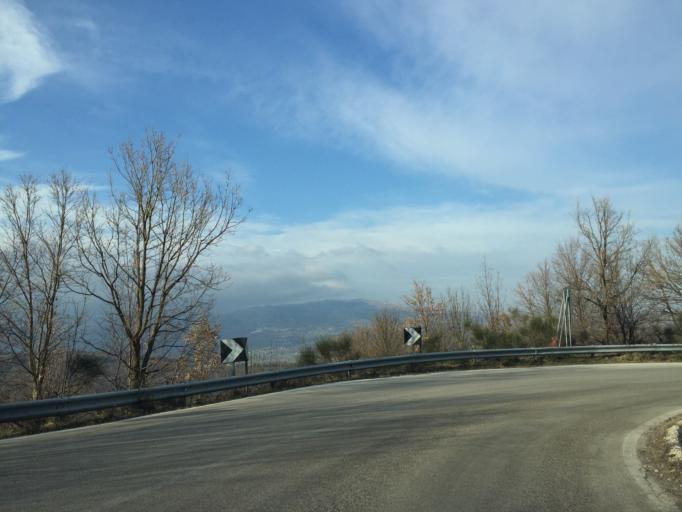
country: IT
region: Molise
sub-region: Provincia di Campobasso
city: San Massimo
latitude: 41.4859
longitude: 14.4081
